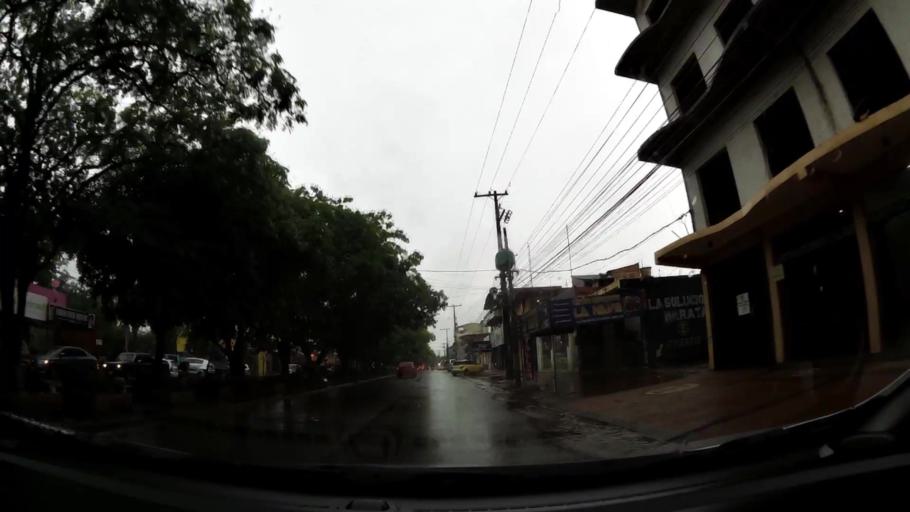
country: PY
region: Alto Parana
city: Ciudad del Este
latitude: -25.5052
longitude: -54.6692
